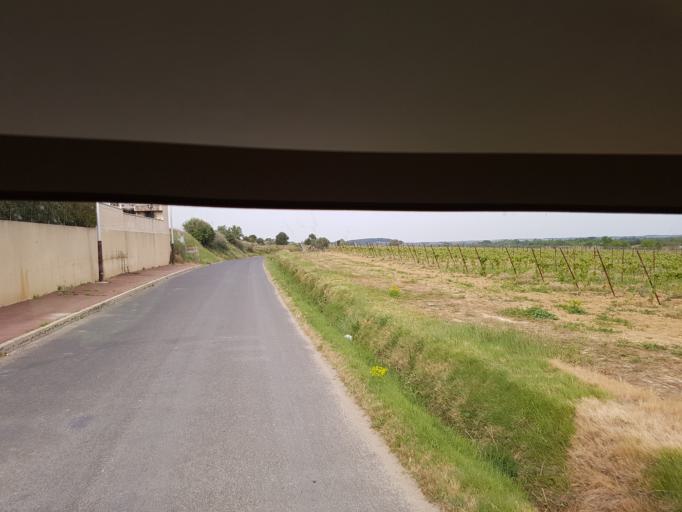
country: FR
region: Languedoc-Roussillon
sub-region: Departement de l'Aude
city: Fleury
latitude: 43.2348
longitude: 3.1410
